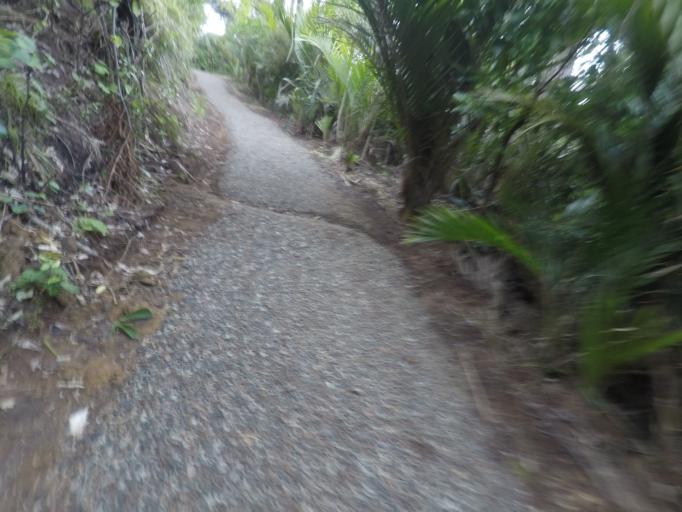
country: NZ
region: Auckland
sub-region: Auckland
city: Muriwai Beach
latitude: -36.9816
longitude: 174.4770
